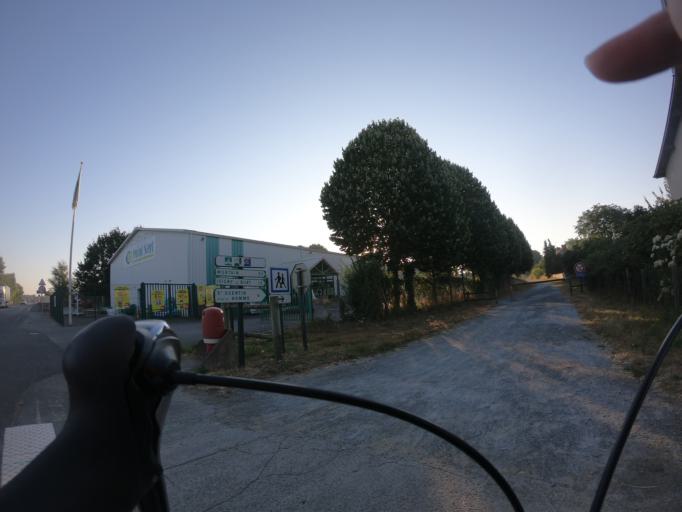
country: FR
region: Lower Normandy
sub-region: Departement de la Manche
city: Ducey
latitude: 48.6236
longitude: -1.2940
